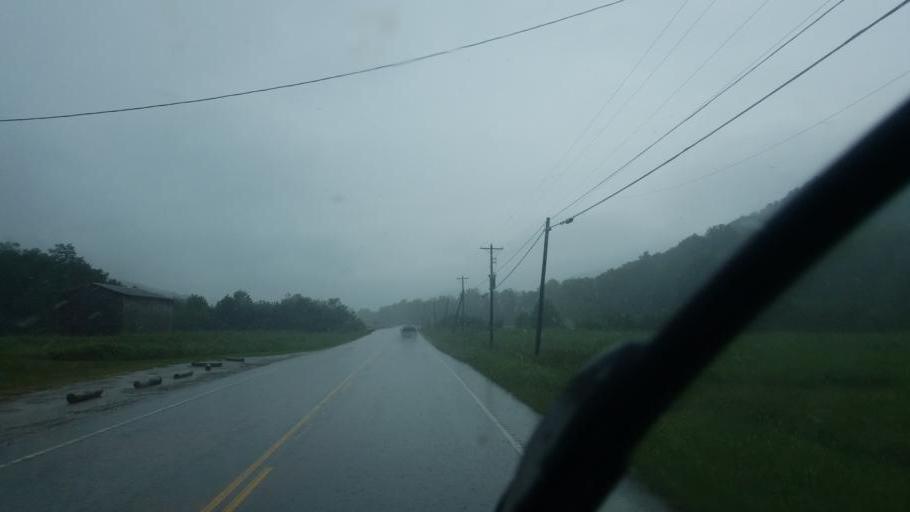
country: US
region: Kentucky
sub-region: Lewis County
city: Vanceburg
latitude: 38.7775
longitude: -83.3327
